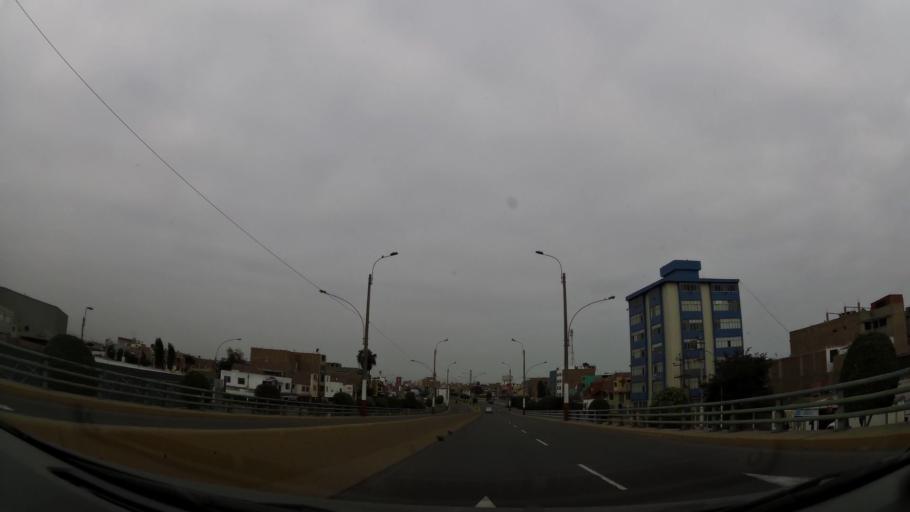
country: PE
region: Callao
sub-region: Callao
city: Callao
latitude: -12.0664
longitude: -77.1180
